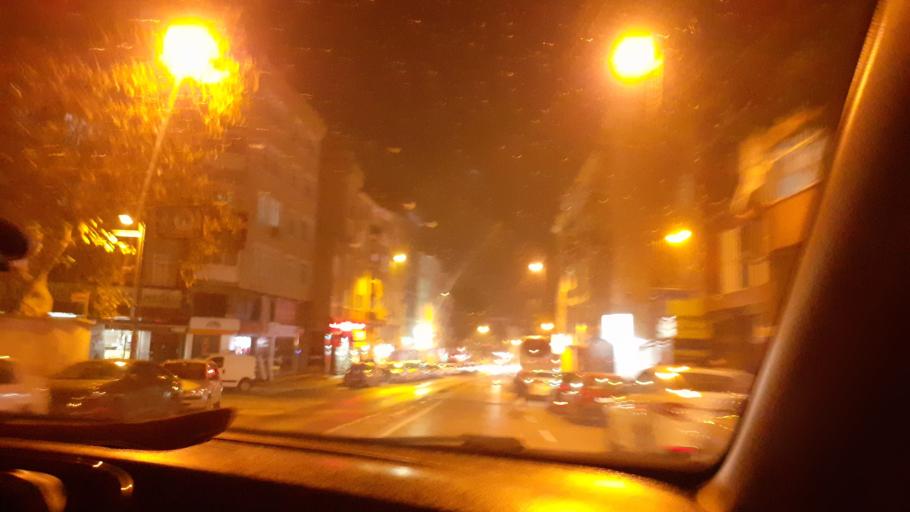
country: TR
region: Istanbul
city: UEskuedar
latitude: 41.0264
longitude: 29.0226
